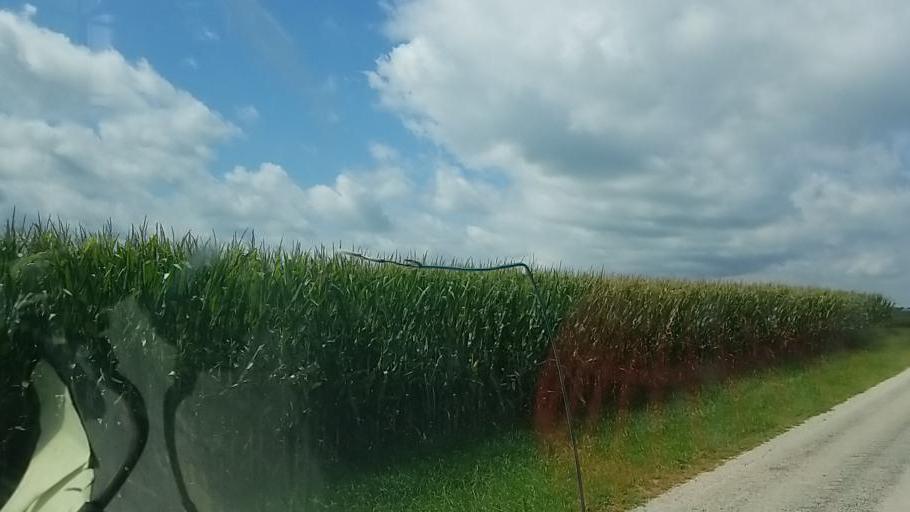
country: US
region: Ohio
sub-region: Madison County
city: Bethel
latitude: 39.7185
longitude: -83.4187
